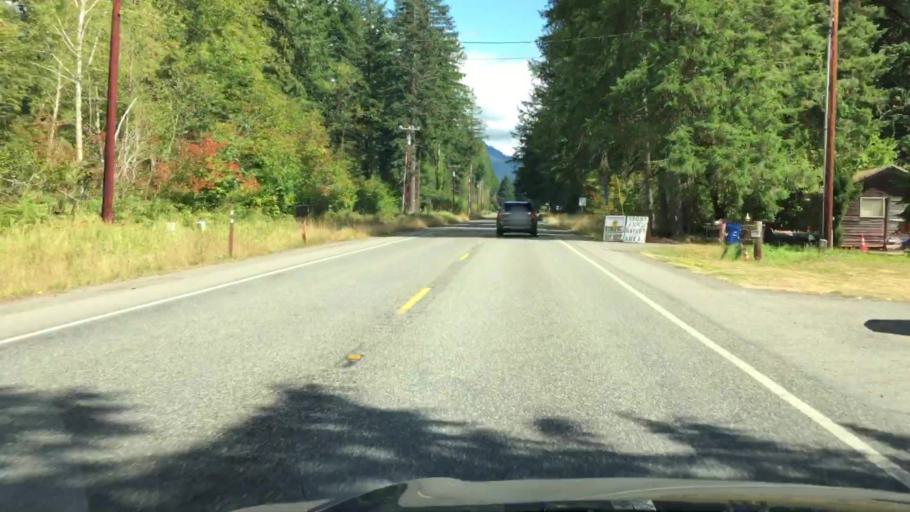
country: US
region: Washington
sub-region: Pierce County
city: Eatonville
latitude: 46.7563
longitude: -122.0707
